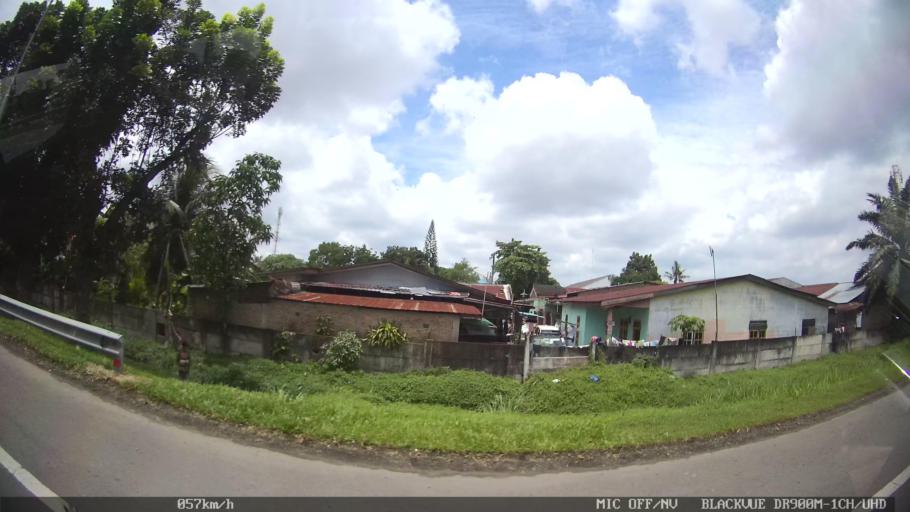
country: ID
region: North Sumatra
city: Medan
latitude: 3.6011
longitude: 98.7235
